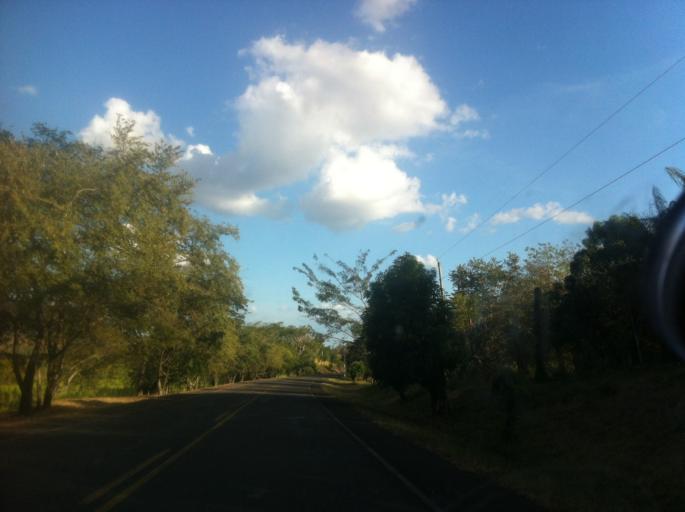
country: NI
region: Chontales
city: Acoyapa
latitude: 11.8538
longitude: -85.0549
